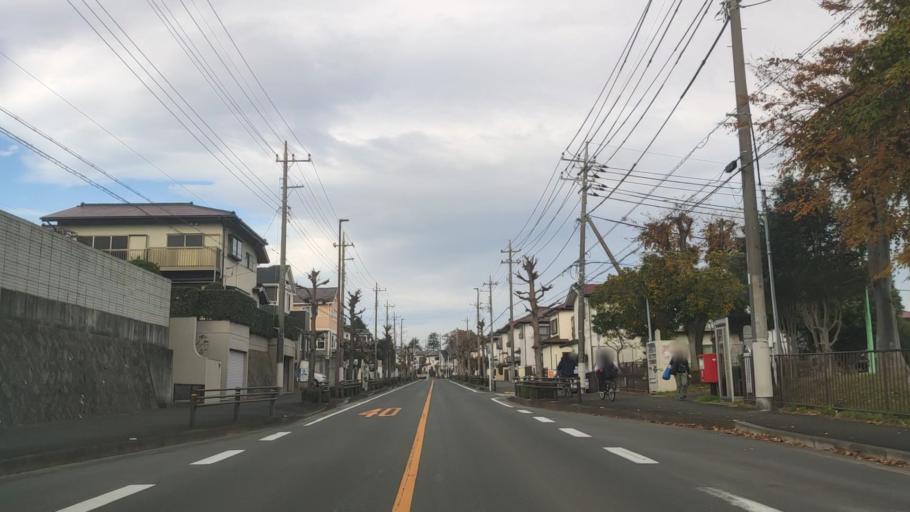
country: JP
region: Kanagawa
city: Atsugi
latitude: 35.4440
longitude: 139.4019
